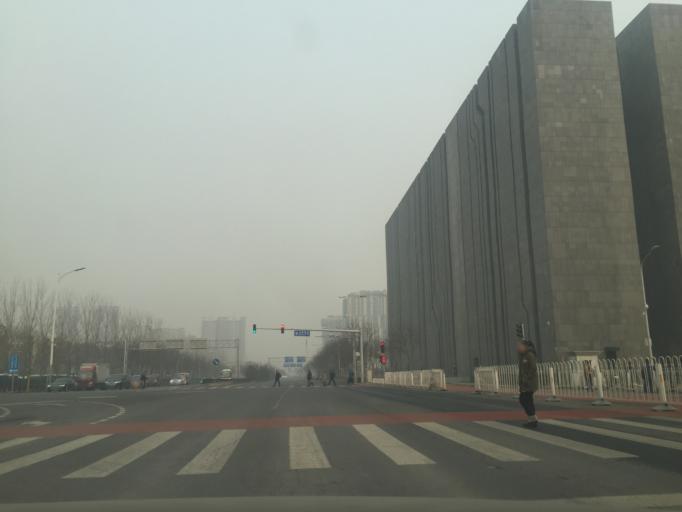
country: CN
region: Beijing
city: Datun
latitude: 39.9927
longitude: 116.3811
